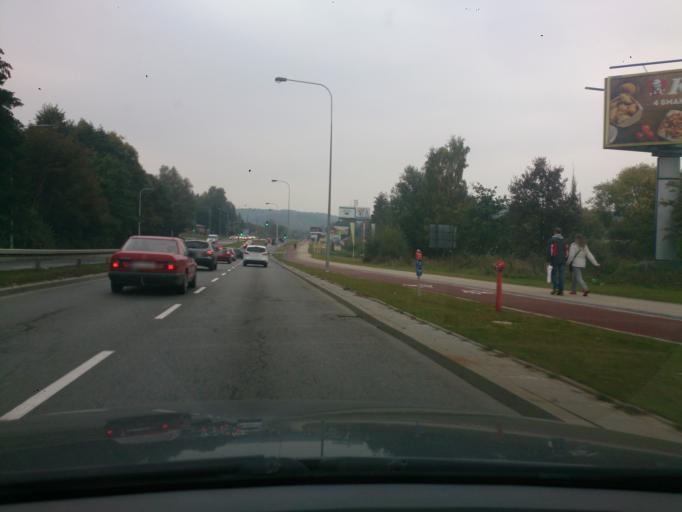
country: PL
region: Pomeranian Voivodeship
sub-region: Powiat gdanski
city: Kowale
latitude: 54.3657
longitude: 18.5724
